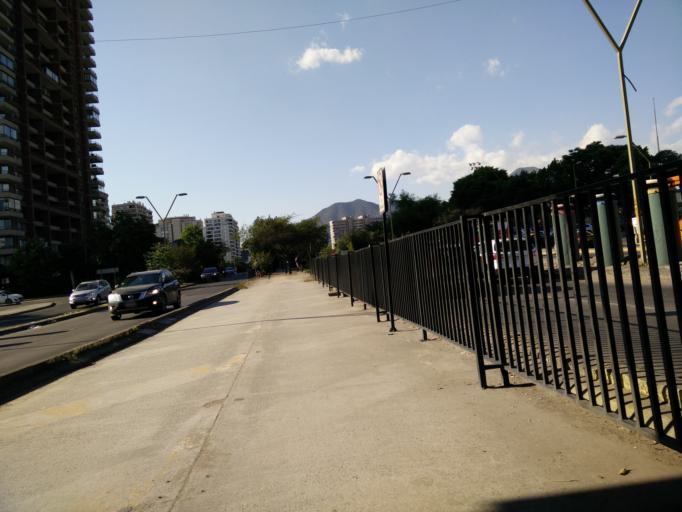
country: CL
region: Santiago Metropolitan
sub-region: Provincia de Santiago
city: Villa Presidente Frei, Nunoa, Santiago, Chile
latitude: -33.4142
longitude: -70.5847
